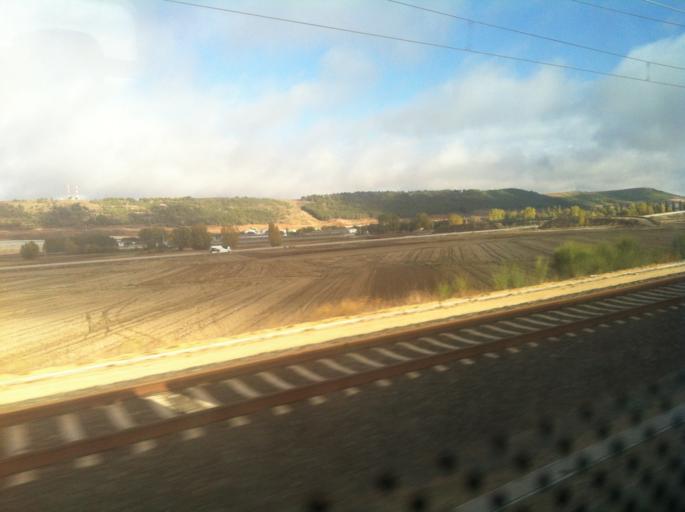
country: ES
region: Castille and Leon
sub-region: Provincia de Burgos
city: Villalbilla de Burgos
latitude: 42.3524
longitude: -3.7783
